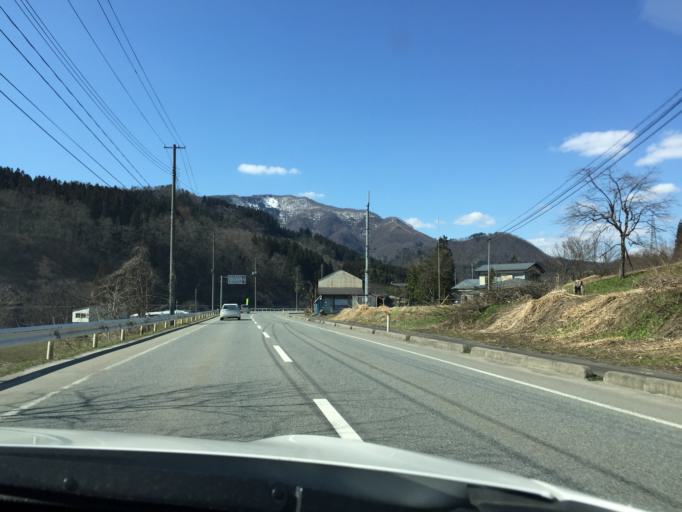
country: JP
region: Yamagata
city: Nagai
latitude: 38.2316
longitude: 140.0913
